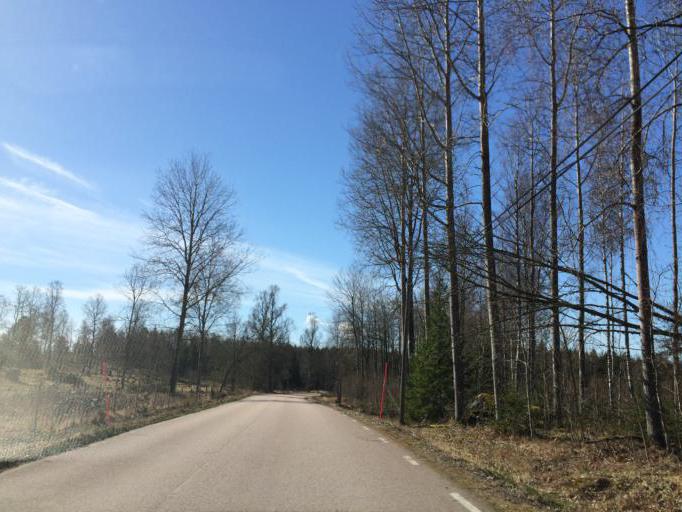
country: SE
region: Soedermanland
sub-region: Eskilstuna Kommun
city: Kvicksund
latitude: 59.5119
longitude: 16.2928
